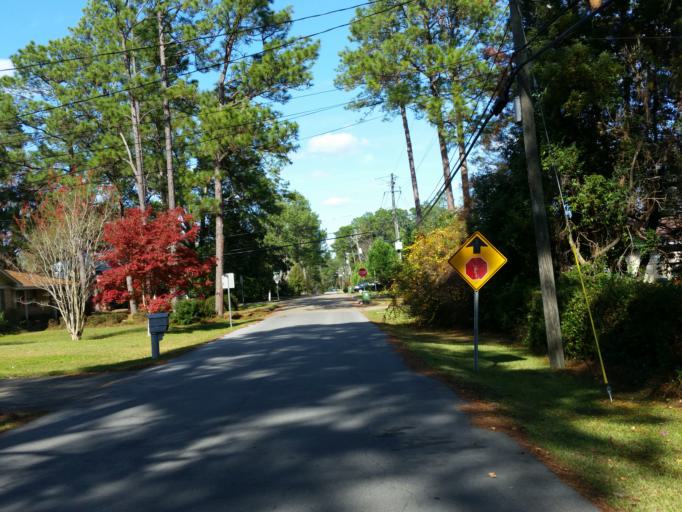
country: US
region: Mississippi
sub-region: Forrest County
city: Hattiesburg
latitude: 31.3114
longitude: -89.3269
